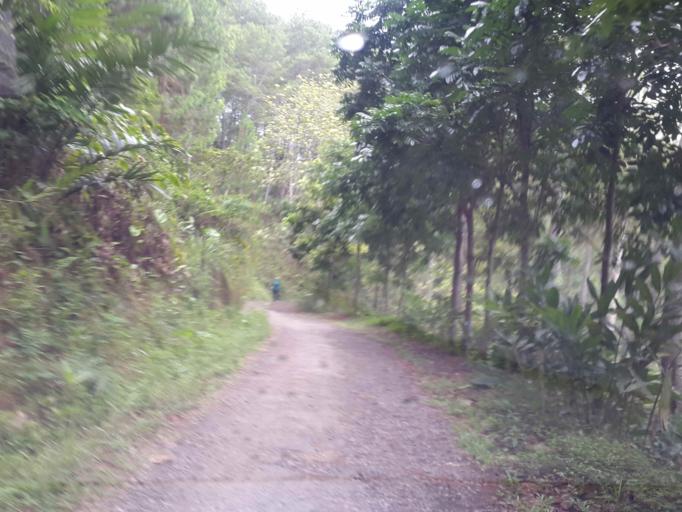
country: ID
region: Central Java
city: Jambuluwuk
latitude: -7.3386
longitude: 108.9563
